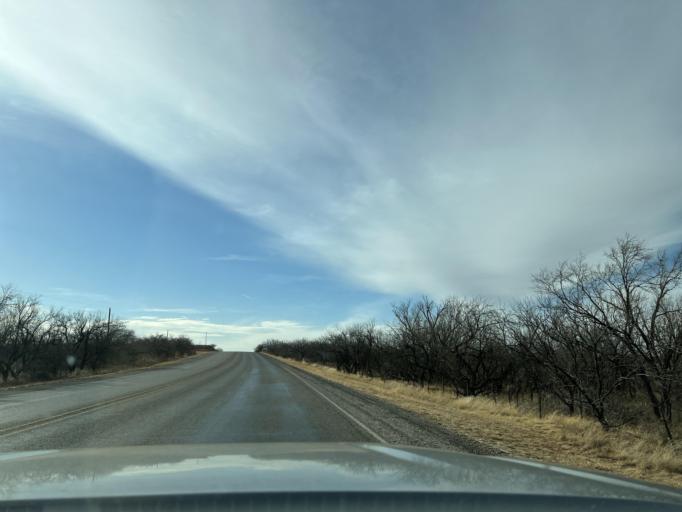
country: US
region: Texas
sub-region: Fisher County
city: Rotan
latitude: 32.7393
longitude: -100.5406
